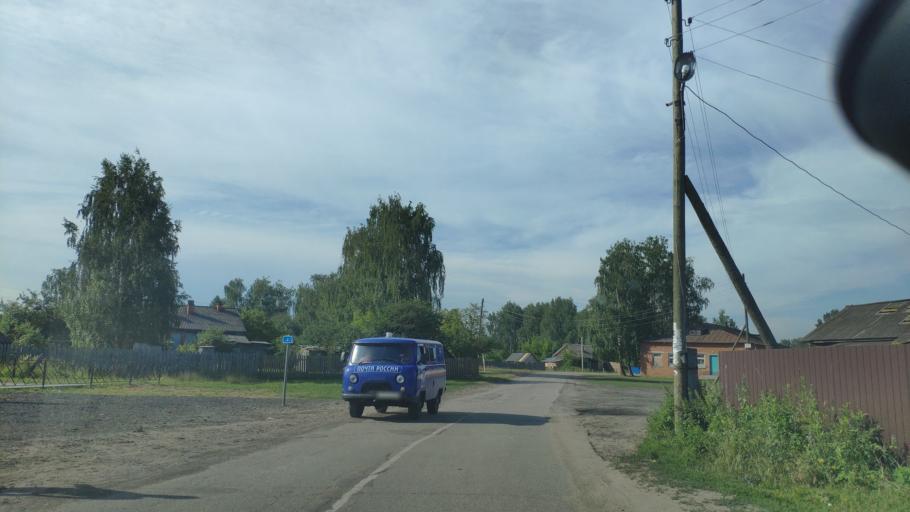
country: RU
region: Nizjnij Novgorod
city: Vorotynets
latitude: 56.1874
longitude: 45.7800
